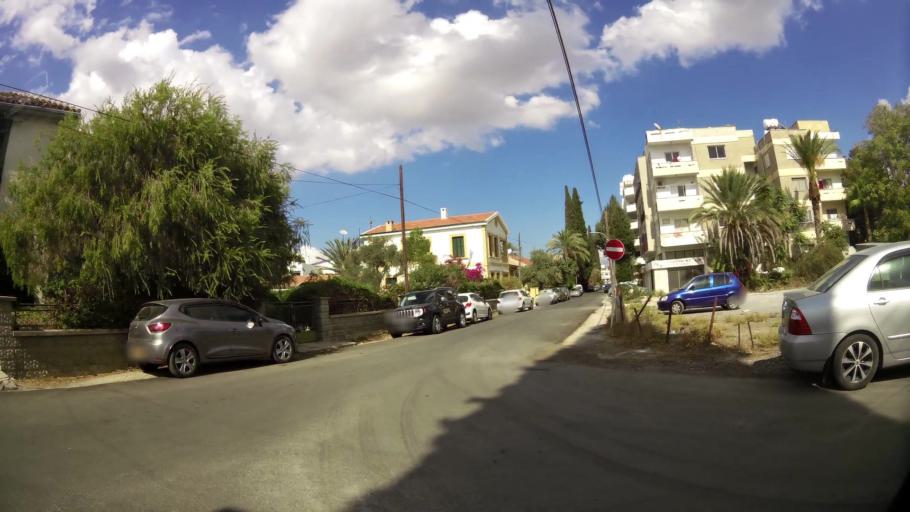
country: CY
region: Lefkosia
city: Nicosia
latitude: 35.1803
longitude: 33.3551
